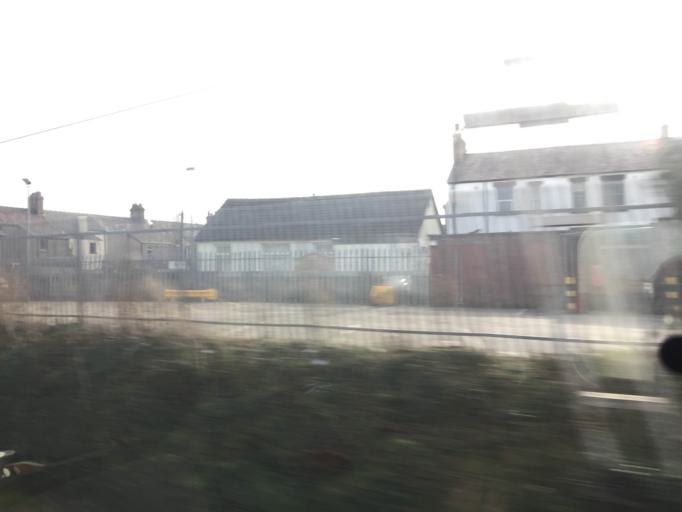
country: GB
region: England
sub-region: Lancashire
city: Carnforth
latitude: 54.1300
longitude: -2.7703
